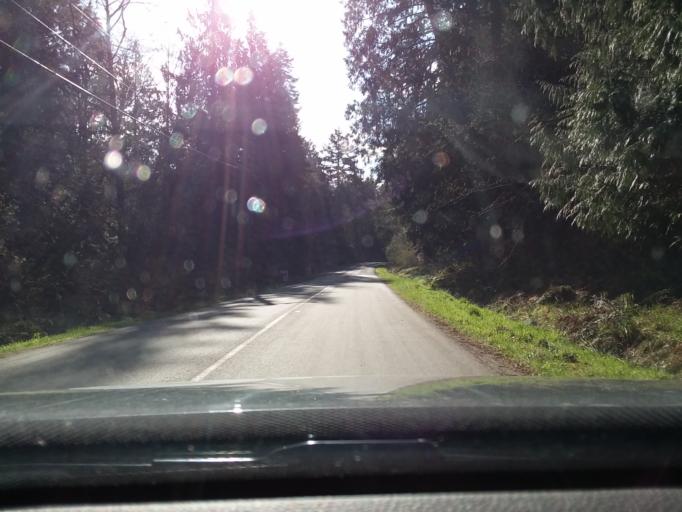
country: CA
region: British Columbia
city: North Cowichan
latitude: 48.9276
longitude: -123.4561
